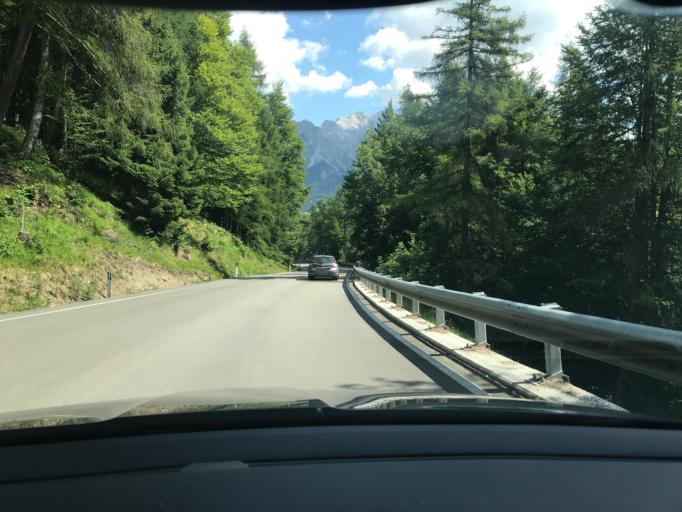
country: IT
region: Veneto
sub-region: Provincia di Belluno
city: Cortina d'Ampezzo
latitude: 46.5269
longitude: 12.1207
